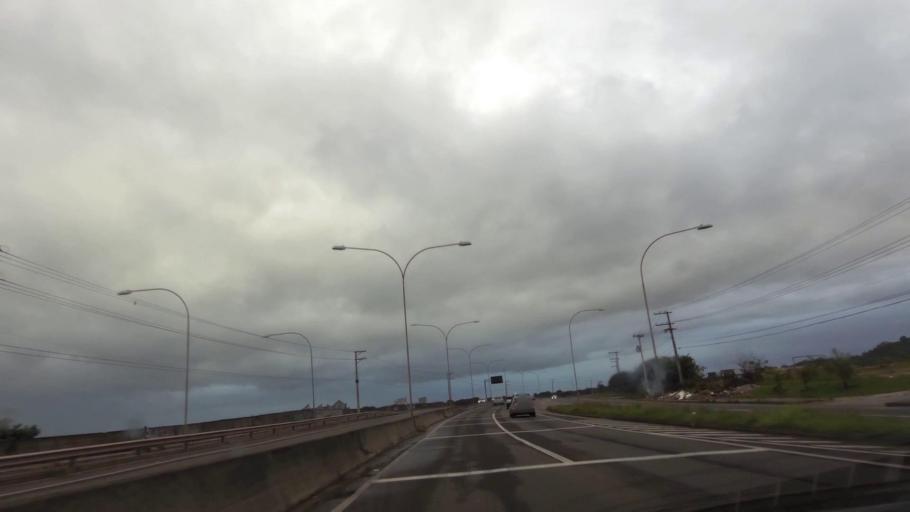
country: BR
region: Espirito Santo
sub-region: Vila Velha
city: Vila Velha
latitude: -20.4489
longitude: -40.3342
